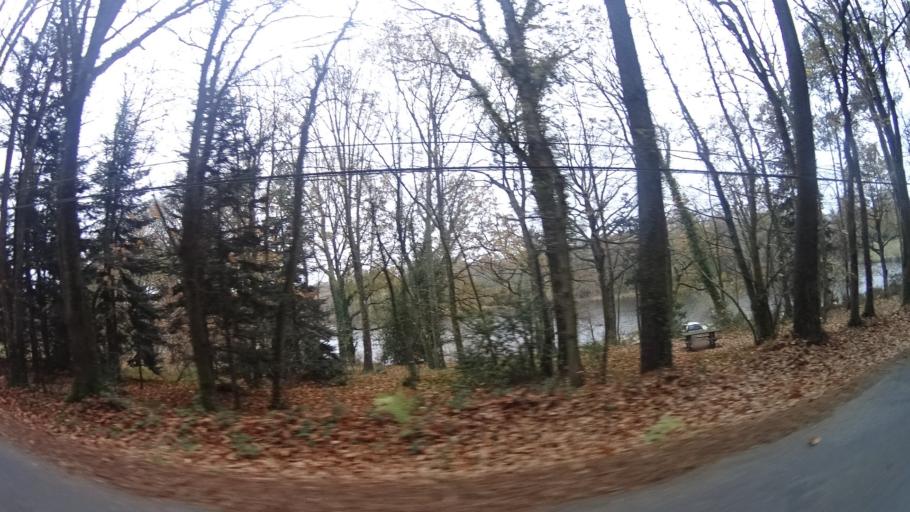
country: FR
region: Brittany
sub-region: Departement d'Ille-et-Vilaine
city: Bains-sur-Oust
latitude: 47.6793
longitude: -2.0818
